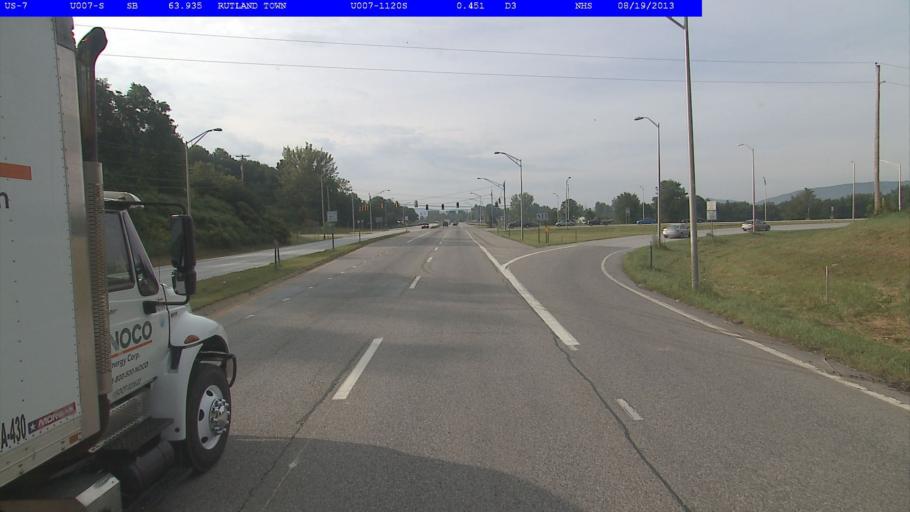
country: US
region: Vermont
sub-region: Rutland County
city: Rutland
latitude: 43.5798
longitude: -72.9671
